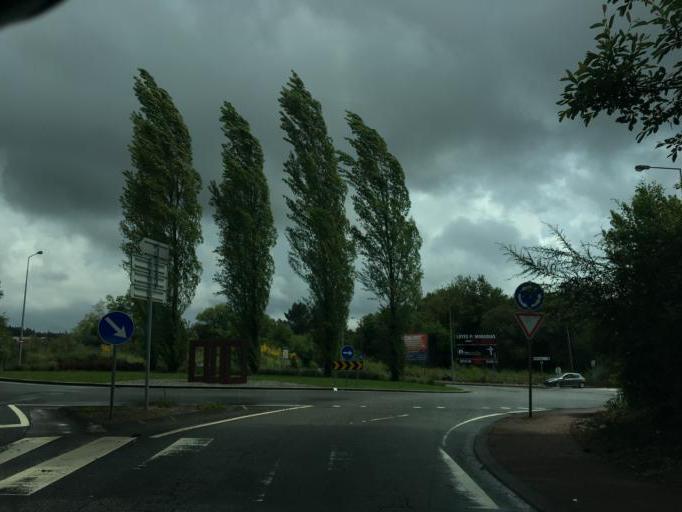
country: PT
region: Porto
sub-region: Maia
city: Nogueira
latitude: 41.2591
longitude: -8.6004
